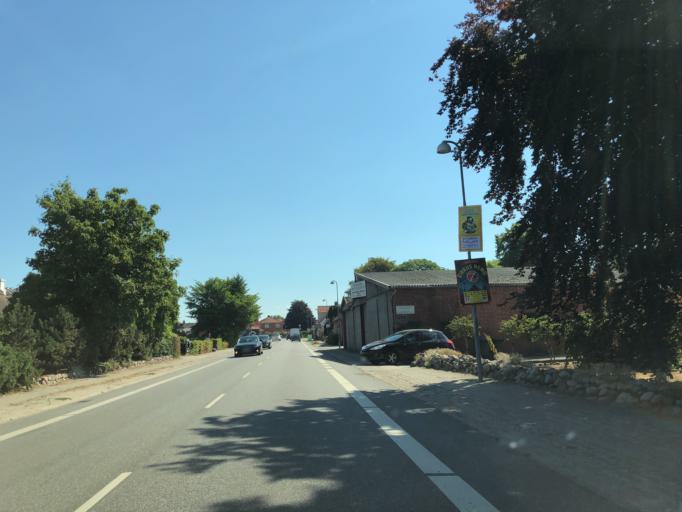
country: DK
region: Zealand
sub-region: Odsherred Kommune
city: Nykobing Sjaelland
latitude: 55.9429
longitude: 11.7487
